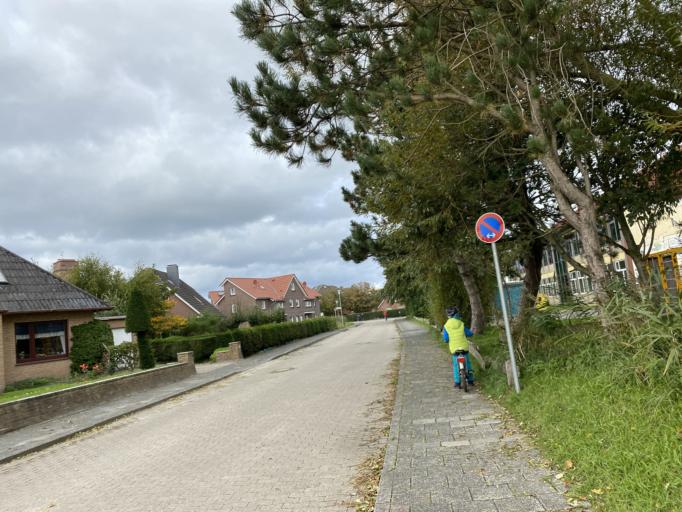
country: DE
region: Lower Saxony
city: Borkum
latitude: 53.5870
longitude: 6.6745
